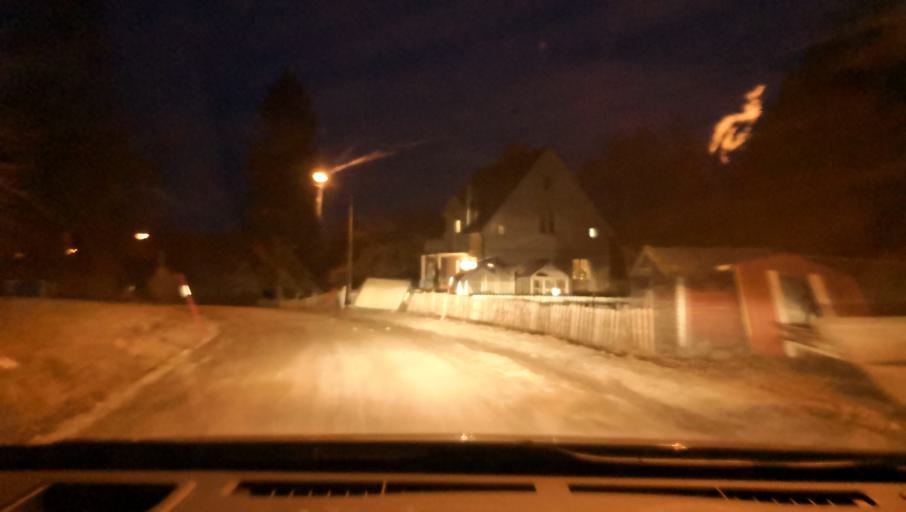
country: SE
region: Vaestmanland
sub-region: Skinnskattebergs Kommun
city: Skinnskatteberg
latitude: 59.6649
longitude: 15.5277
